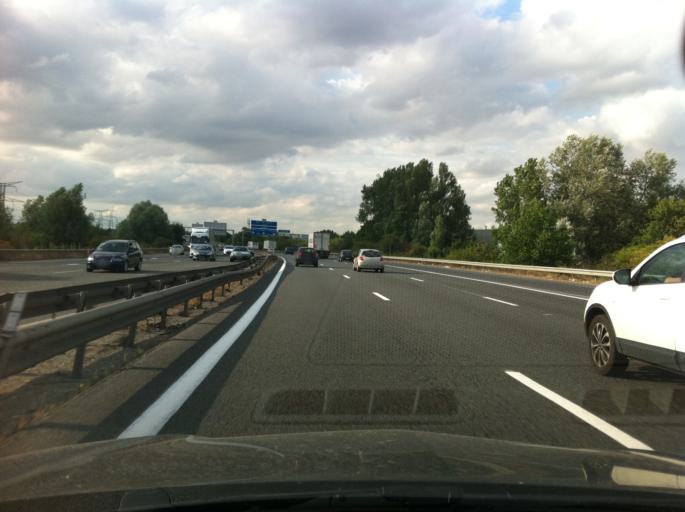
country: FR
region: Ile-de-France
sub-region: Departement de Seine-et-Marne
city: Saint-Thibault-des-Vignes
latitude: 48.8699
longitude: 2.6705
